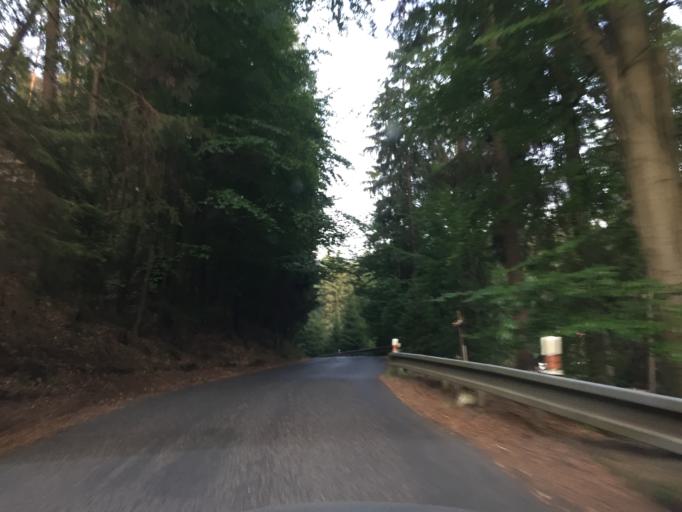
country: CZ
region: Ustecky
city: Ceska Kamenice
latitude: 50.8535
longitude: 14.3754
